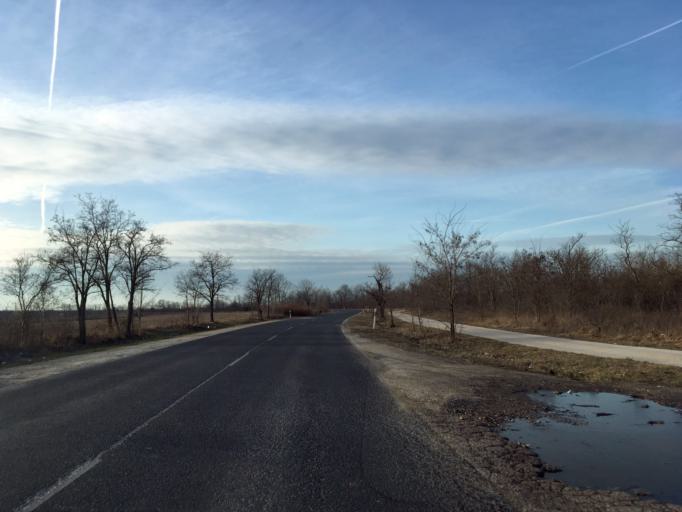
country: AT
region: Burgenland
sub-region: Politischer Bezirk Neusiedl am See
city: Nickelsdorf
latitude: 47.9250
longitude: 17.1270
